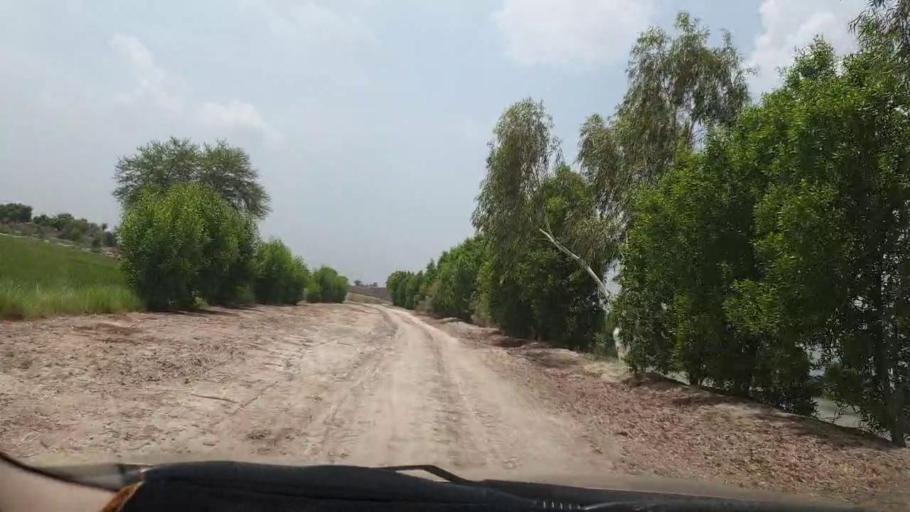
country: PK
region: Sindh
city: Larkana
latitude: 27.6146
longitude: 68.1539
